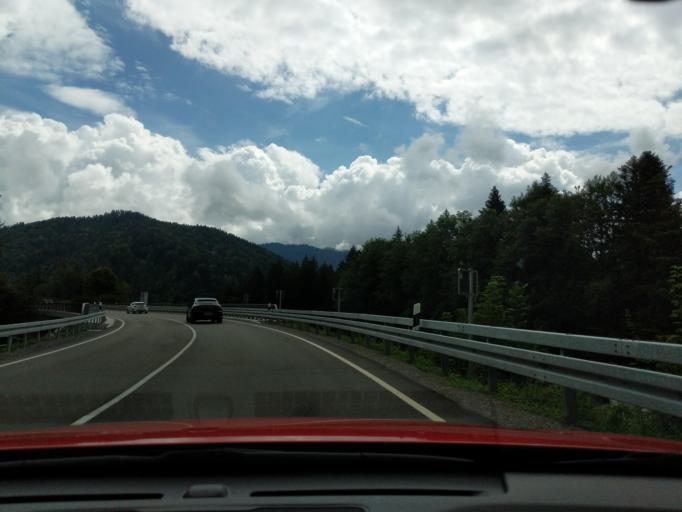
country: DE
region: Bavaria
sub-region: Swabia
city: Oberstaufen
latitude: 47.5494
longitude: 10.0277
